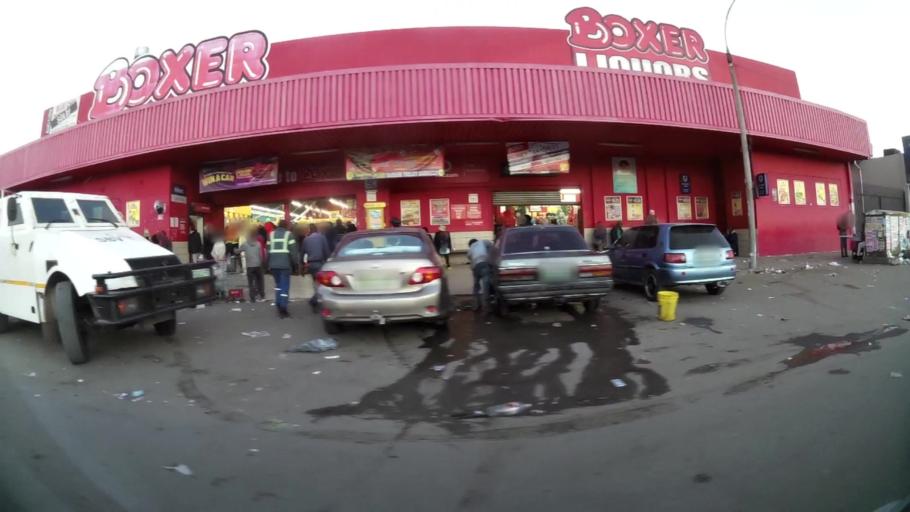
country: ZA
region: North-West
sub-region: Bojanala Platinum District Municipality
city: Rustenburg
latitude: -25.6622
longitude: 27.2382
